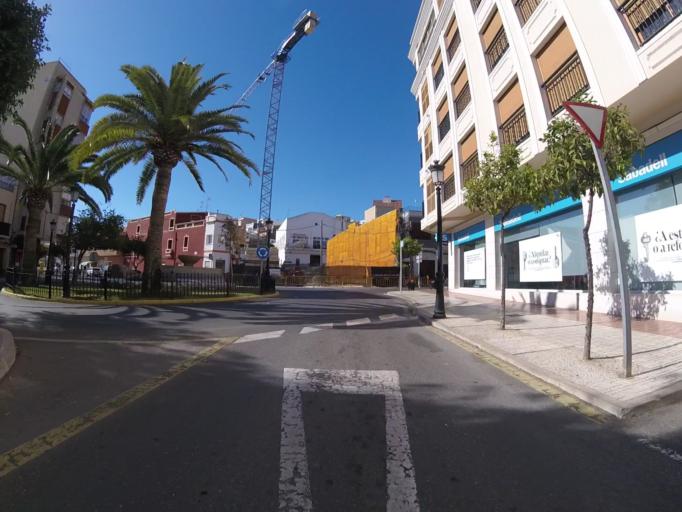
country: ES
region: Valencia
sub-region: Provincia de Castello
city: Orpesa/Oropesa del Mar
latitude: 40.0938
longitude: 0.1354
